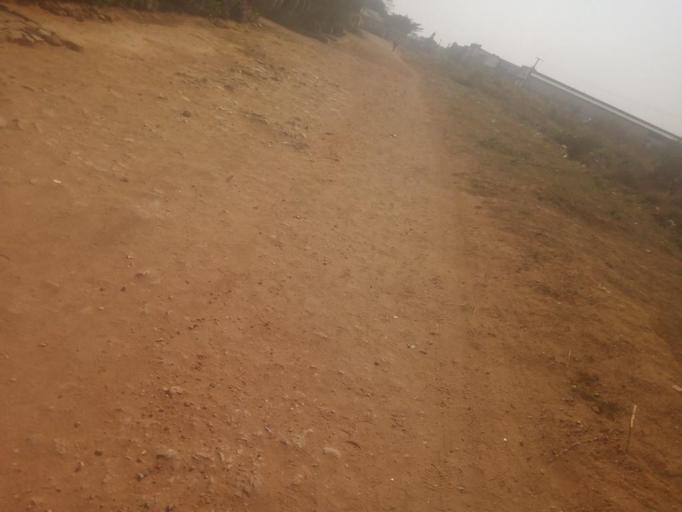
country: ZM
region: Lusaka
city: Lusaka
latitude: -15.3999
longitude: 28.3920
